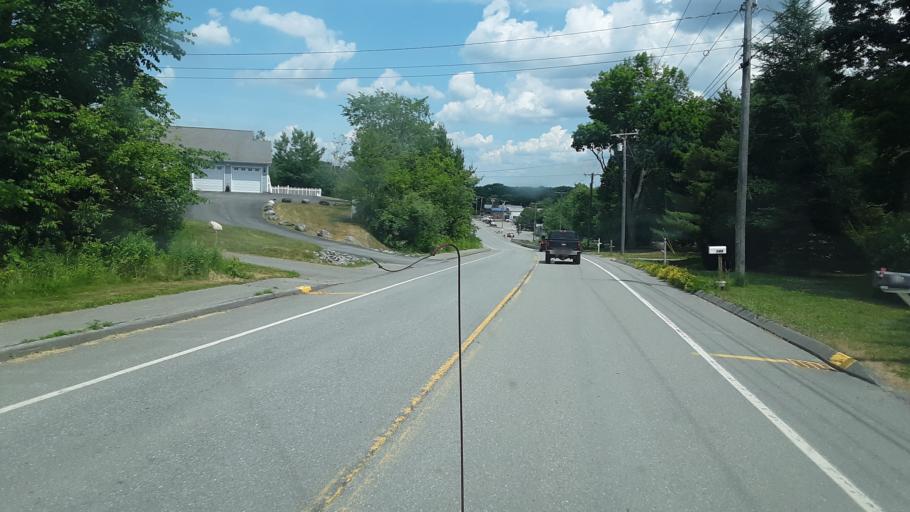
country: US
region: Maine
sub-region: Penobscot County
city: Hampden
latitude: 44.7648
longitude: -68.8028
